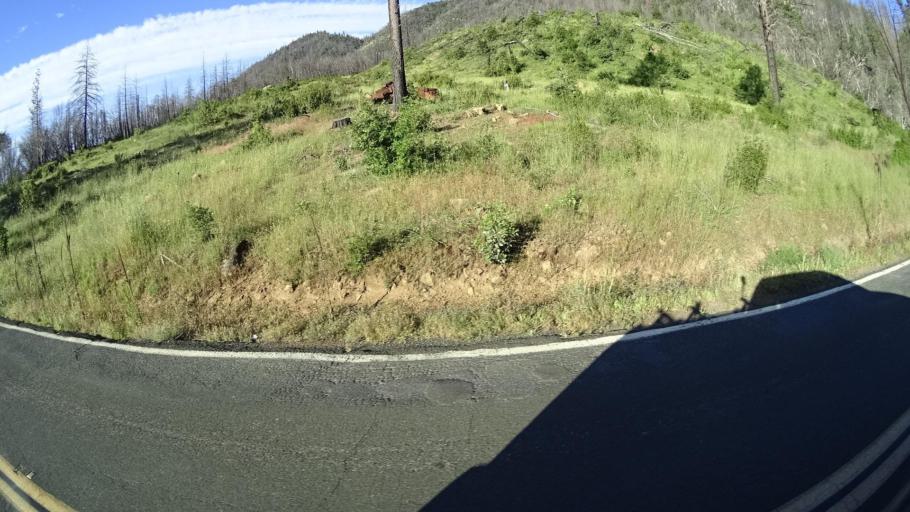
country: US
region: California
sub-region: Lake County
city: Upper Lake
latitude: 39.2454
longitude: -122.9486
